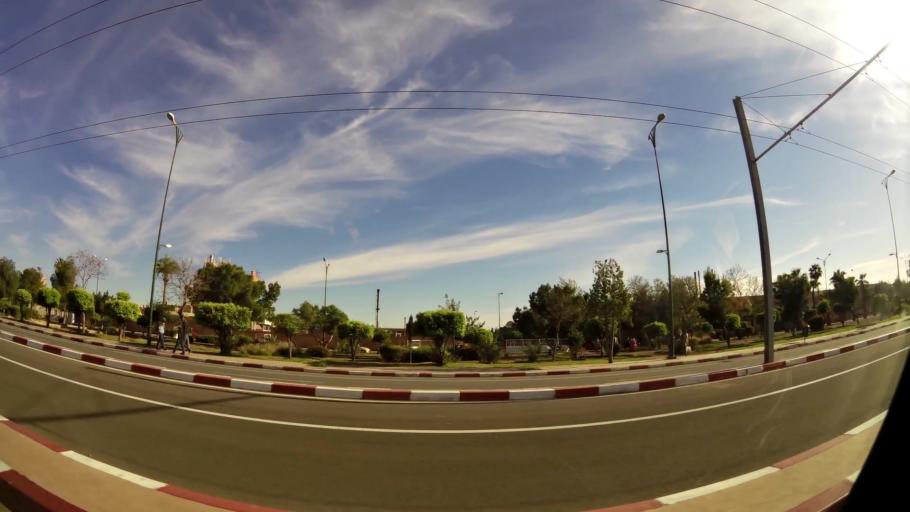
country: MA
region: Marrakech-Tensift-Al Haouz
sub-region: Marrakech
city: Marrakesh
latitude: 31.6280
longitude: -8.0498
